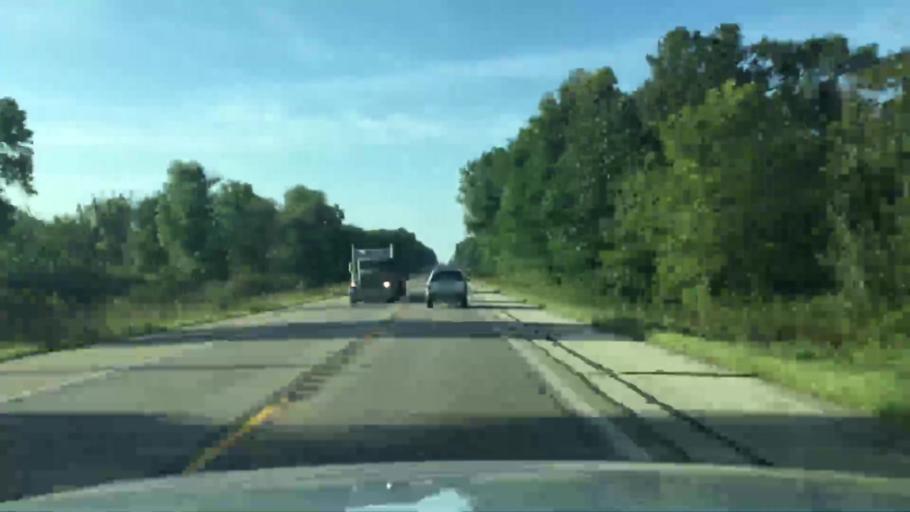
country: US
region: Michigan
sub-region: Jackson County
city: Vandercook Lake
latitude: 42.0954
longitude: -84.3639
